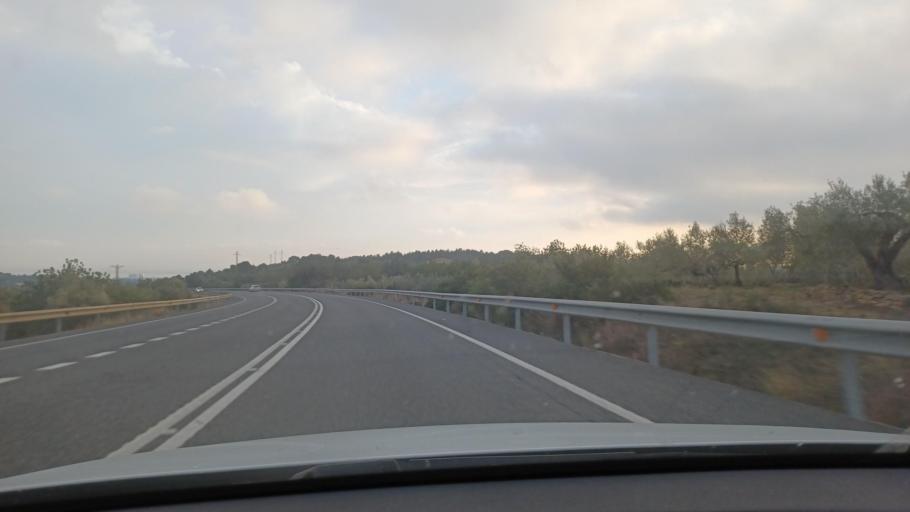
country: ES
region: Catalonia
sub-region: Provincia de Tarragona
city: El Perello
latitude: 40.8534
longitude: 0.7125
